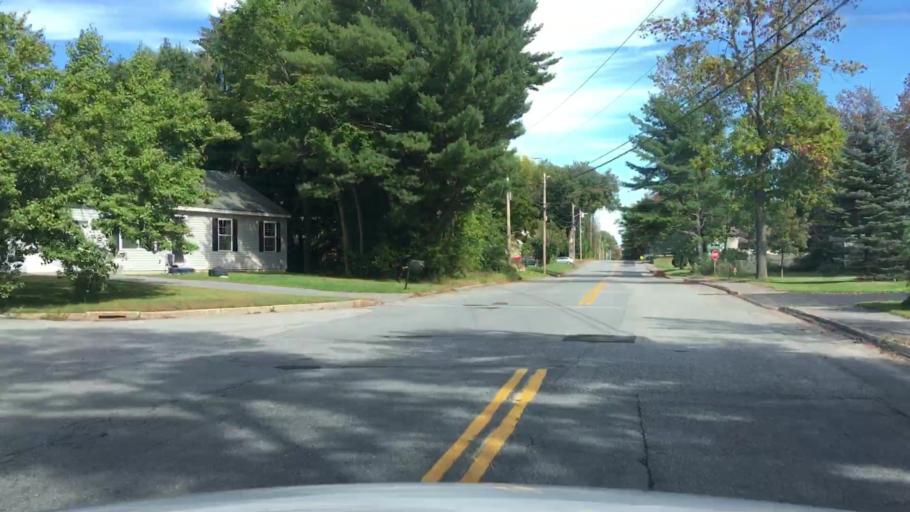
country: US
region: Maine
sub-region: Cumberland County
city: Westbrook
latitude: 43.6744
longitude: -70.3850
